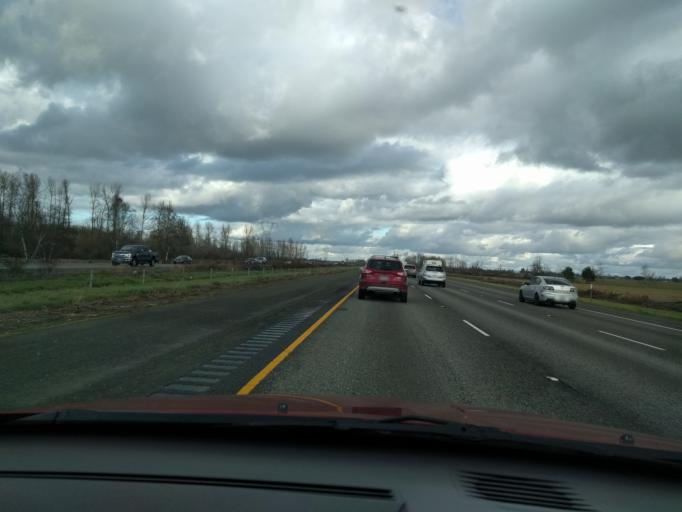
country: US
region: Oregon
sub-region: Marion County
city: Gervais
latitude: 45.1012
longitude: -122.9313
